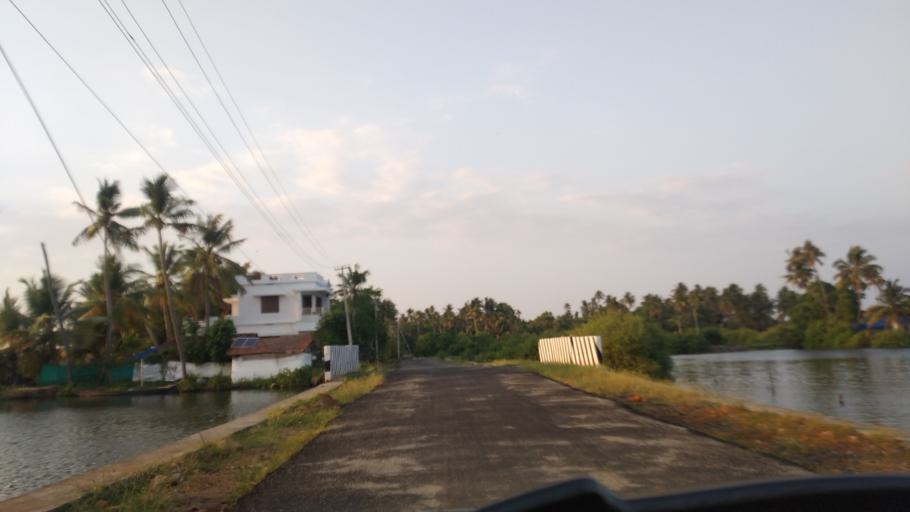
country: IN
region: Kerala
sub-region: Ernakulam
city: Elur
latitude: 10.0534
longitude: 76.2263
